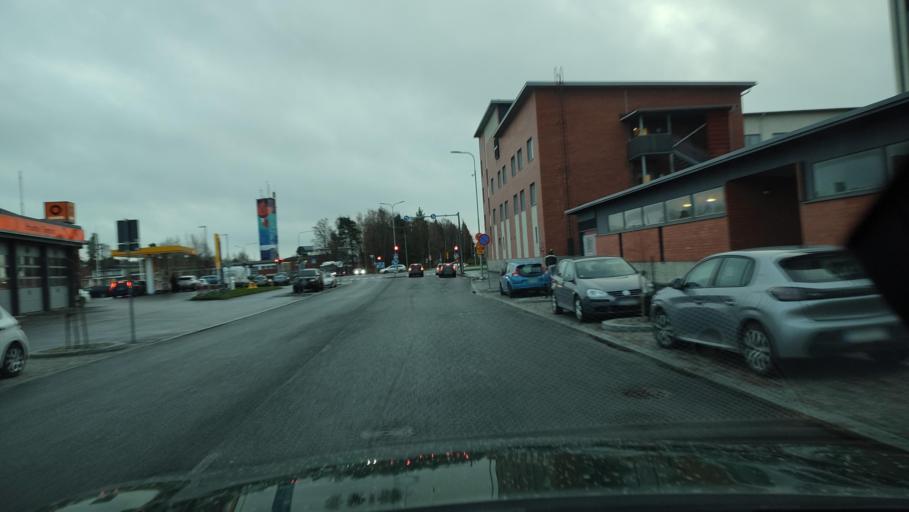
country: FI
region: Ostrobothnia
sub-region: Vaasa
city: Vaasa
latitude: 63.1012
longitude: 21.6347
